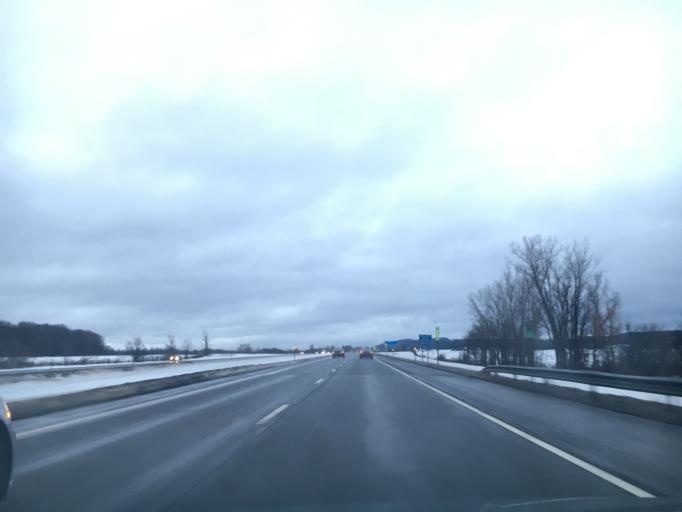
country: US
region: New York
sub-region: Cortland County
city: Homer
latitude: 42.7782
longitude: -76.1265
